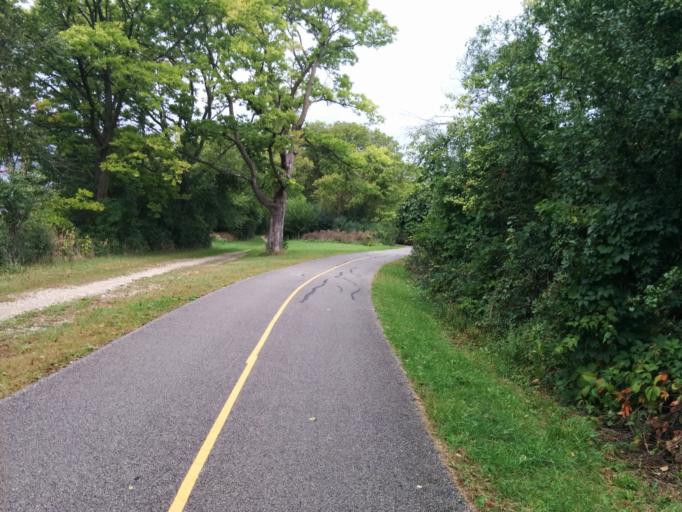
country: US
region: Illinois
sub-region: Cook County
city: Northfield
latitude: 42.1101
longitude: -87.7733
